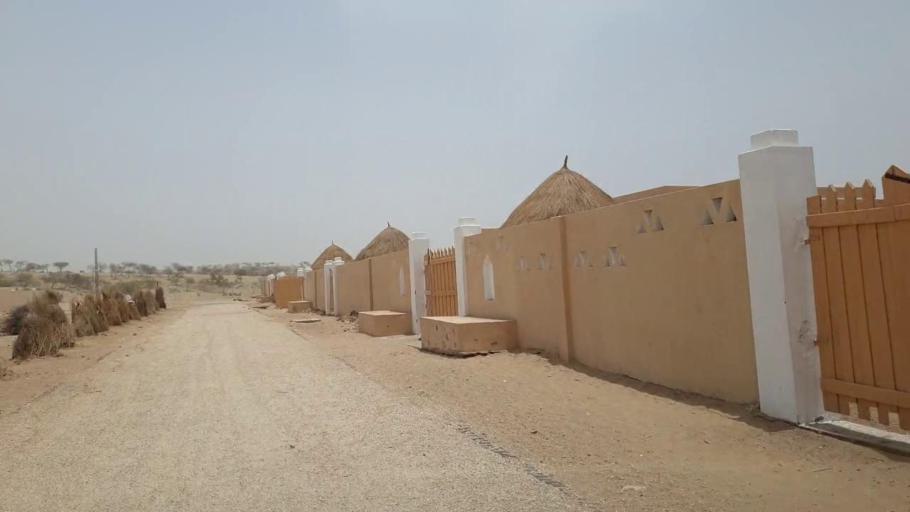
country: PK
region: Sindh
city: Islamkot
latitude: 24.7237
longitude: 70.3323
